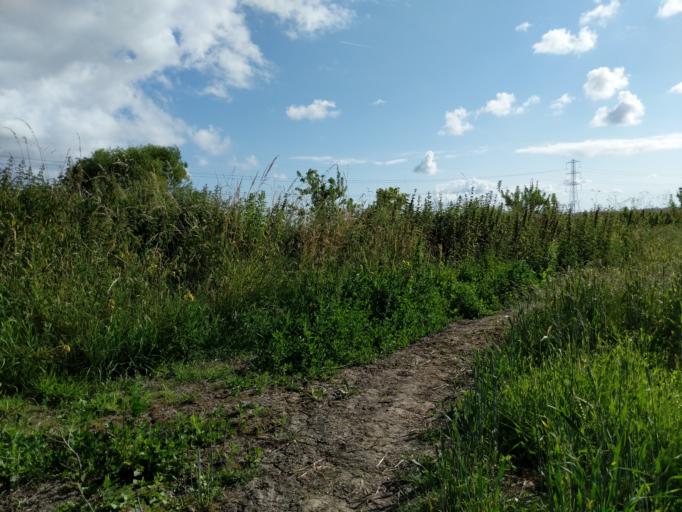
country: GB
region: England
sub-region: Kent
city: Dunkirk
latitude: 51.3351
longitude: 0.9483
